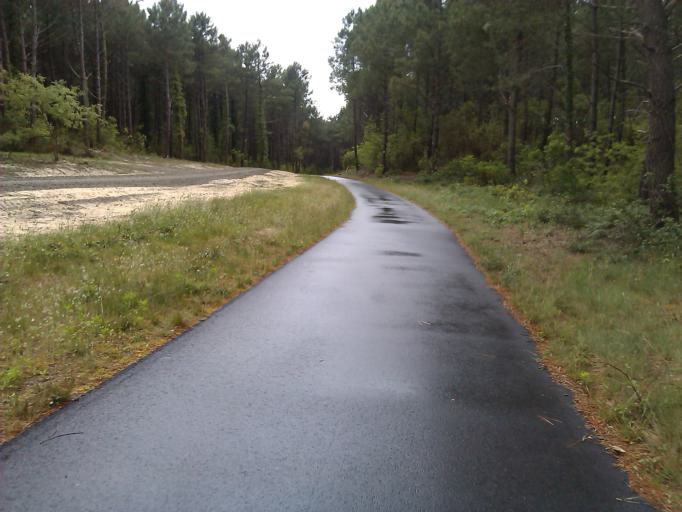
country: FR
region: Aquitaine
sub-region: Departement des Landes
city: Vielle-Saint-Girons
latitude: 43.9257
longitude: -1.3537
